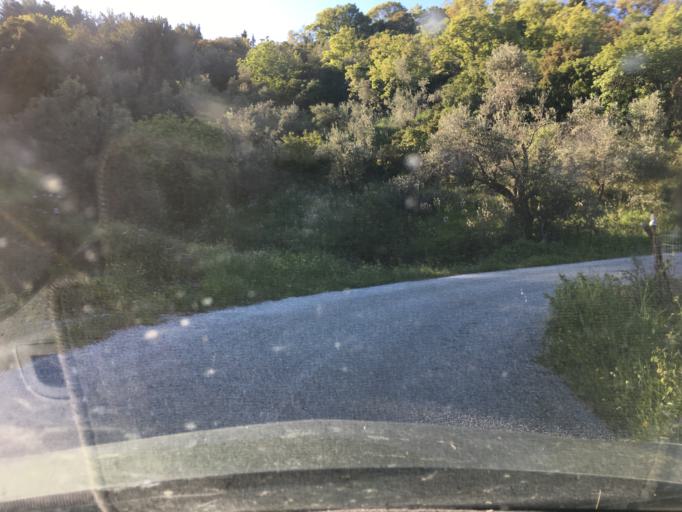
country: GR
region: Thessaly
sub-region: Nomos Magnisias
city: Skopelos
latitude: 39.1776
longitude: 23.6204
